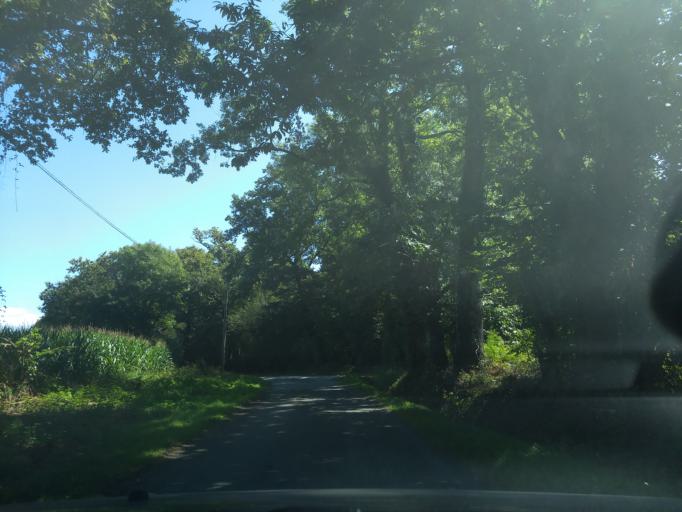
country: FR
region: Aquitaine
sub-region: Departement des Pyrenees-Atlantiques
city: Soumoulou
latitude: 43.2825
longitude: -0.1431
